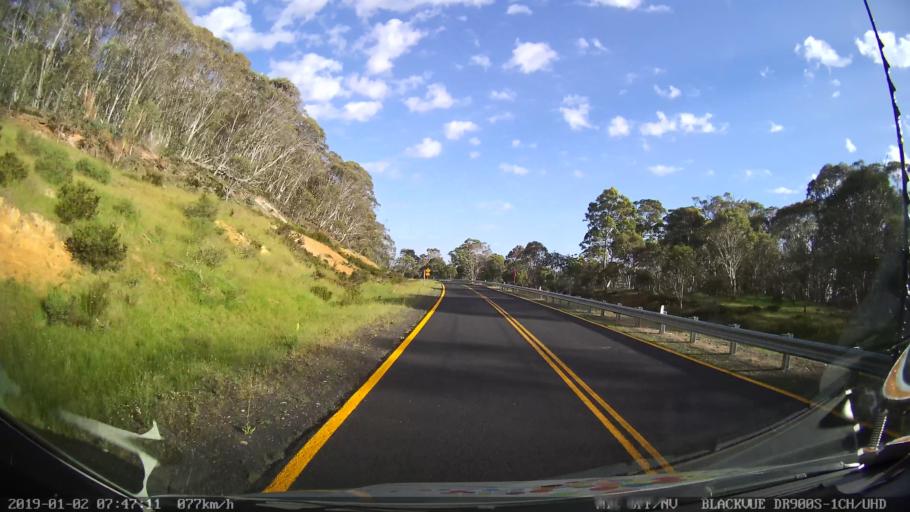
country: AU
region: New South Wales
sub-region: Tumut Shire
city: Tumut
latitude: -35.7675
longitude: 148.5216
